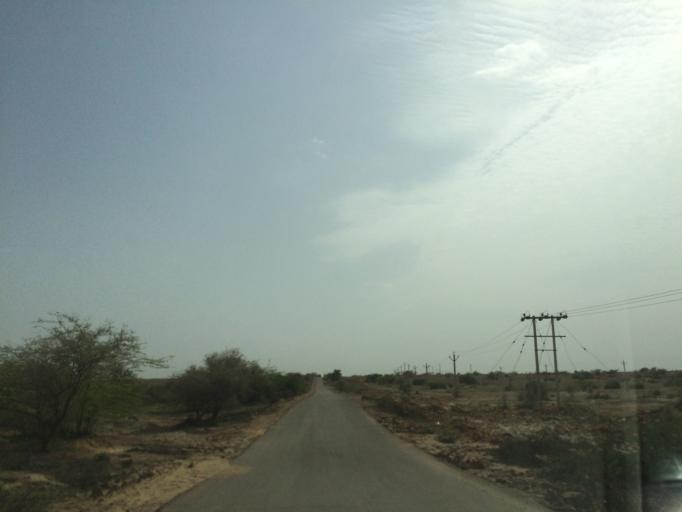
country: IN
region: Rajasthan
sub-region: Jaisalmer
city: Jaisalmer
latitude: 26.8877
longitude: 70.9156
